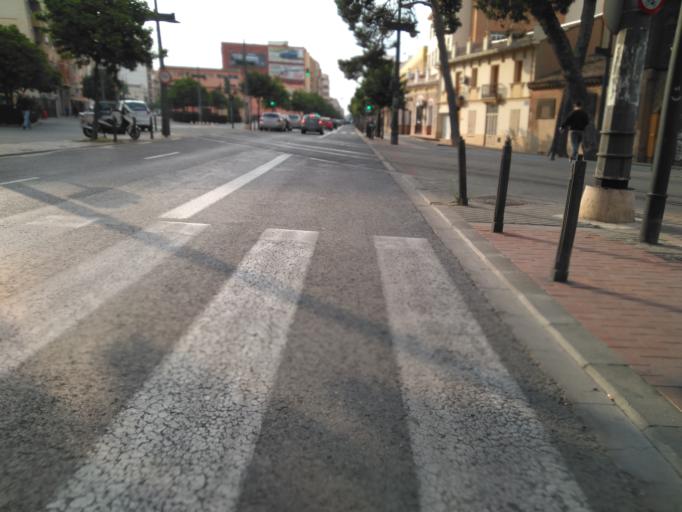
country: ES
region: Valencia
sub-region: Provincia de Valencia
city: Valencia
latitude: 39.4900
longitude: -0.3910
